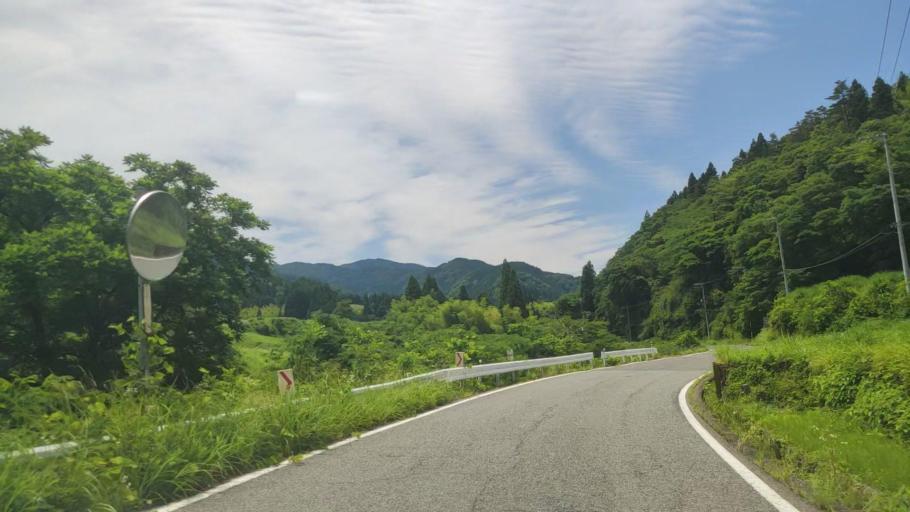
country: JP
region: Tottori
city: Tottori
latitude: 35.4297
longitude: 134.5300
